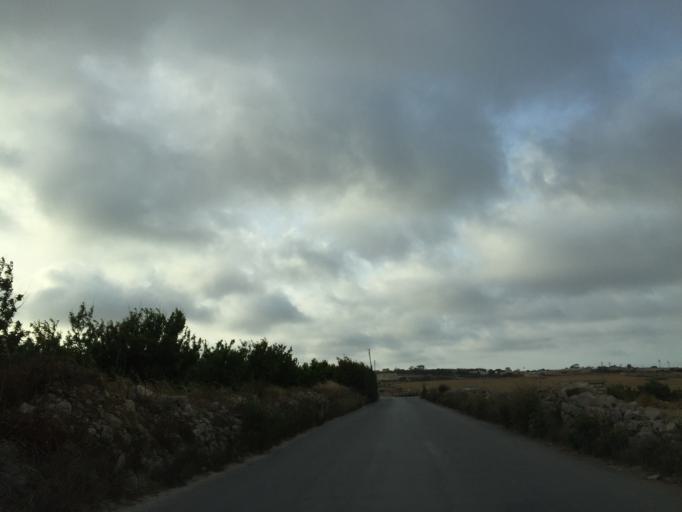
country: MT
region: L-Imdina
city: Imdina
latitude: 35.8754
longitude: 14.4133
